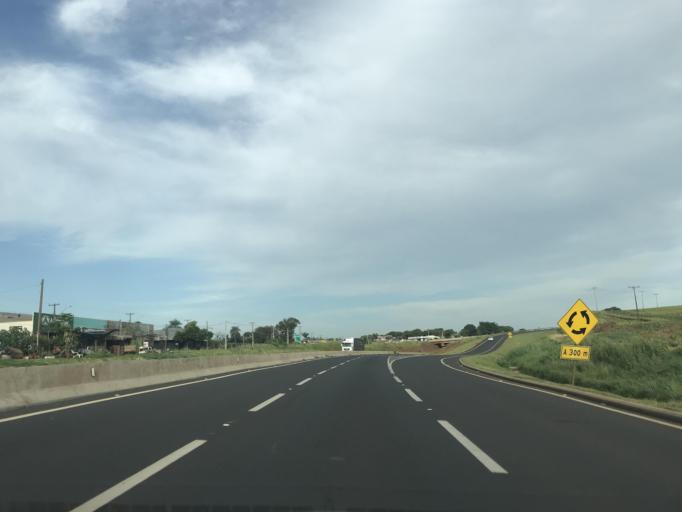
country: BR
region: Parana
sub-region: Mandaguacu
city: Mandaguacu
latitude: -23.3378
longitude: -52.1045
